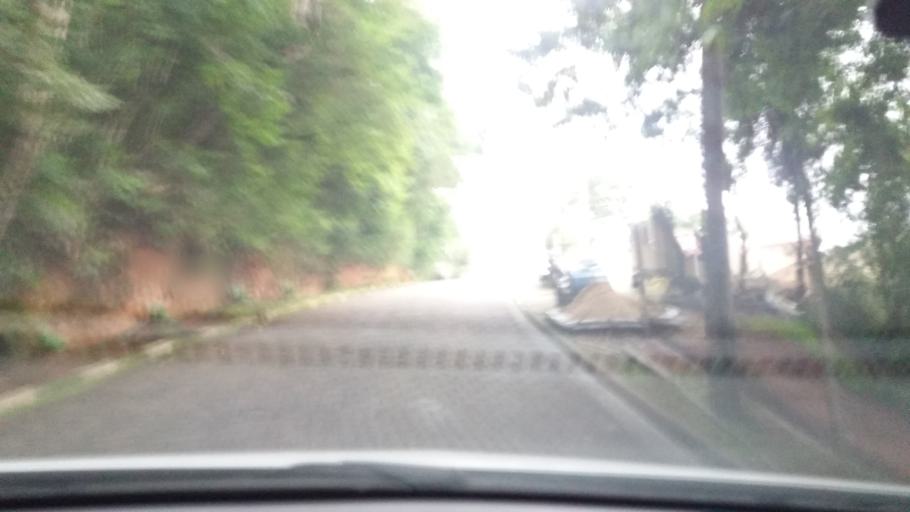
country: BR
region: Sao Paulo
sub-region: Bom Jesus Dos Perdoes
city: Bom Jesus dos Perdoes
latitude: -23.1700
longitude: -46.4623
